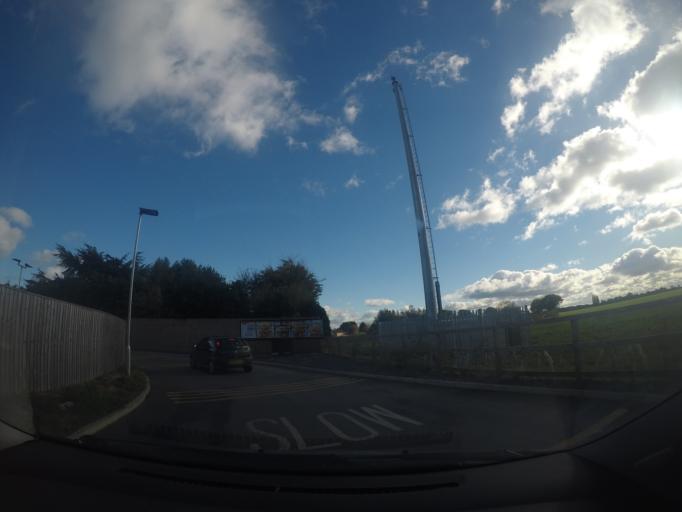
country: GB
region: England
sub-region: City of York
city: Nether Poppleton
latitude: 53.9713
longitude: -1.1439
